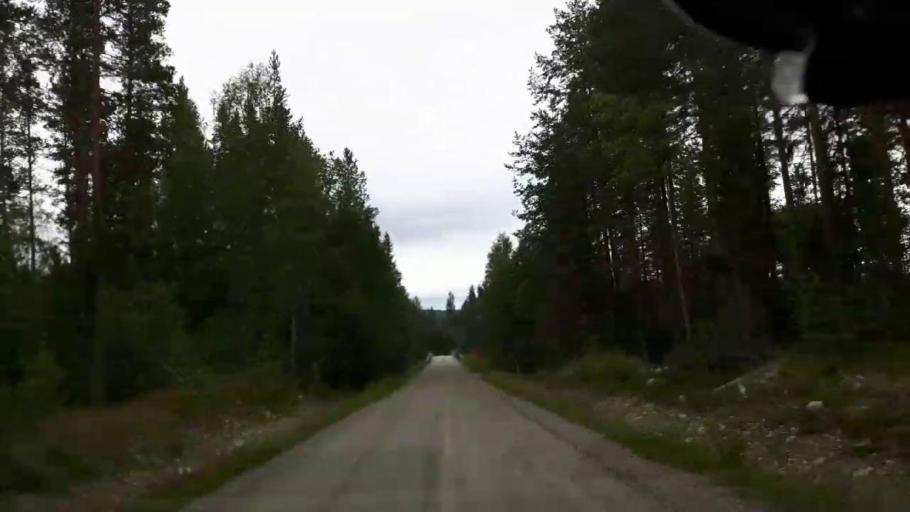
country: SE
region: Vaesternorrland
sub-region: Ange Kommun
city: Ange
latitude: 62.8192
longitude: 15.7137
